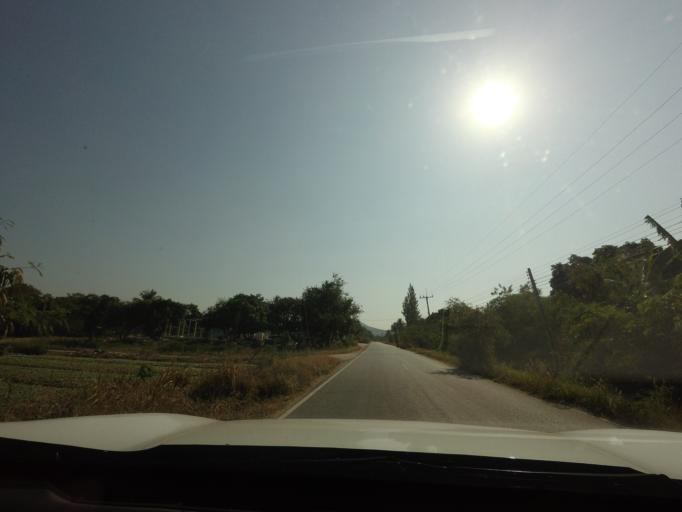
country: TH
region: Nakhon Ratchasima
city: Pak Chong
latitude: 14.6161
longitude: 101.4864
